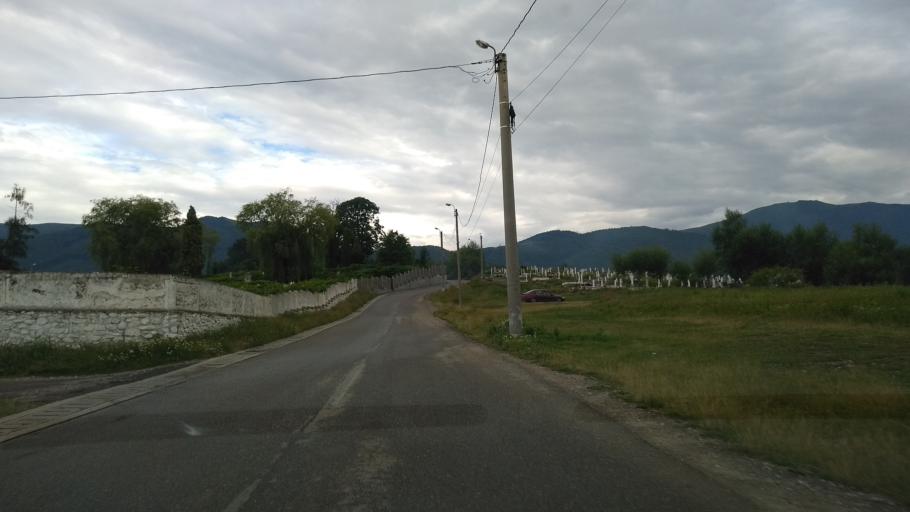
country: RO
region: Hunedoara
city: Vulcan
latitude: 45.3693
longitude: 23.2824
